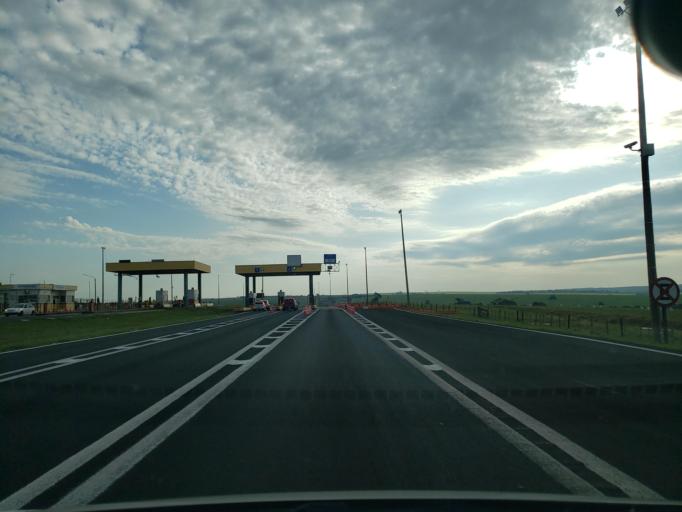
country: BR
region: Sao Paulo
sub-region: Guararapes
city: Guararapes
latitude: -21.2103
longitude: -50.7313
